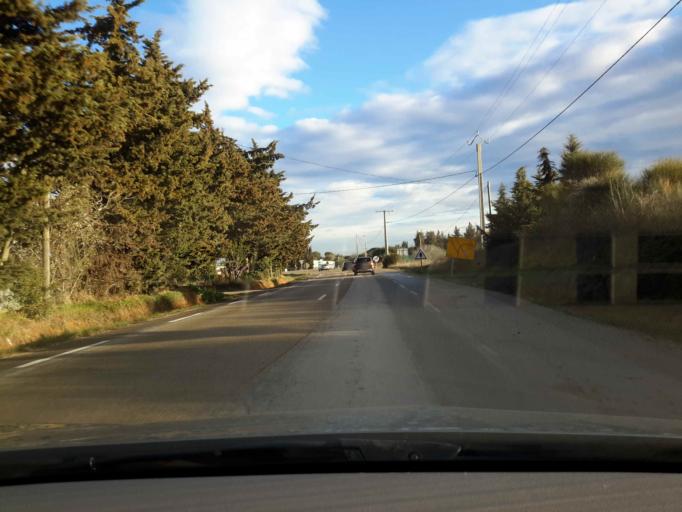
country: FR
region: Languedoc-Roussillon
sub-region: Departement du Gard
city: Generac
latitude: 43.7515
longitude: 4.3425
